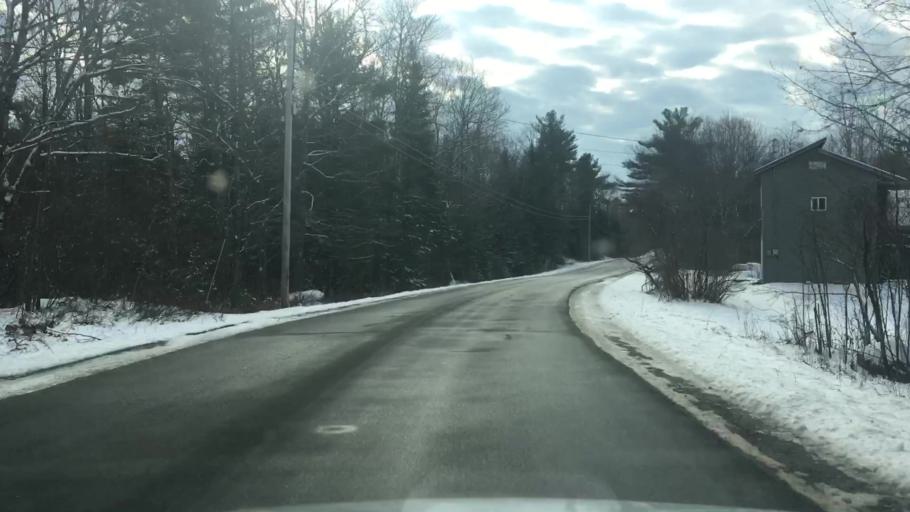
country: US
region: Maine
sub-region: Kennebec County
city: Chelsea
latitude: 44.2850
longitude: -69.6666
